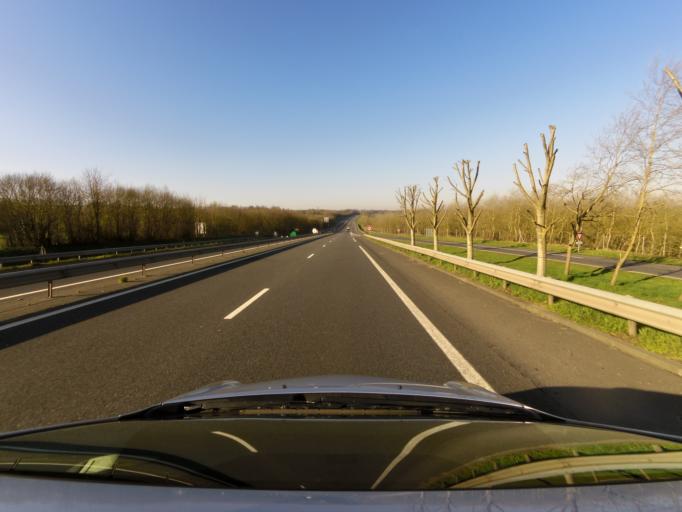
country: FR
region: Lower Normandy
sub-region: Departement du Calvados
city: Saint-Martin-des-Besaces
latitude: 49.0246
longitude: -0.8344
